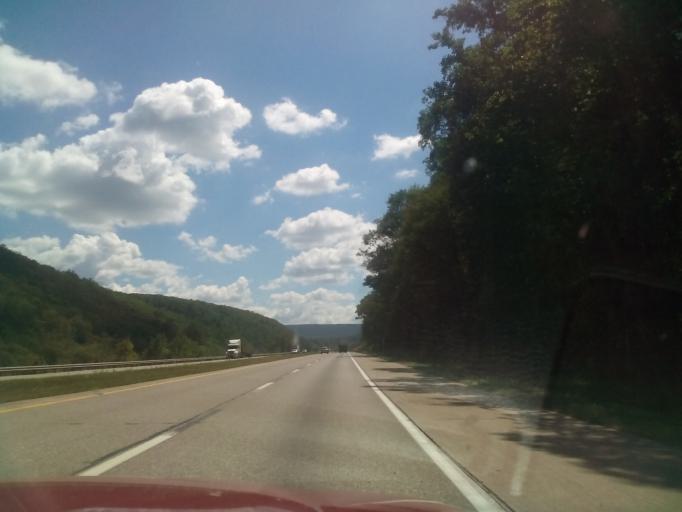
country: US
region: Pennsylvania
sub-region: Luzerne County
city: Nescopeck
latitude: 41.0150
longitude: -76.1683
